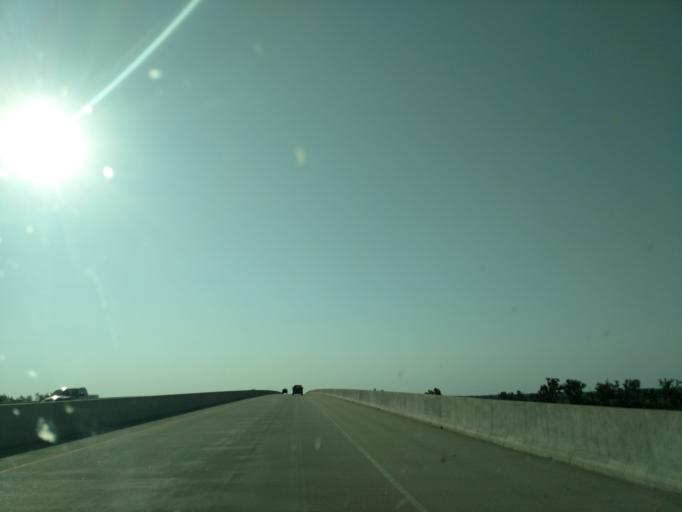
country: US
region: Nebraska
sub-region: Cass County
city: Plattsmouth
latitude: 41.0664
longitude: -95.8756
